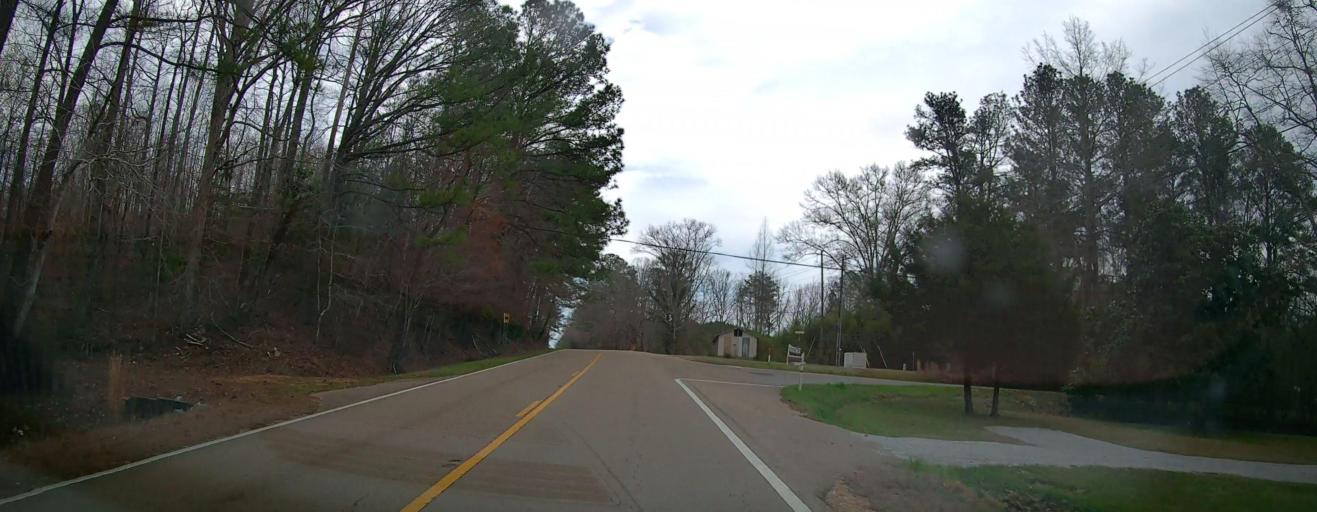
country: US
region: Mississippi
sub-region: Itawamba County
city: Fulton
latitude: 34.2494
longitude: -88.2999
